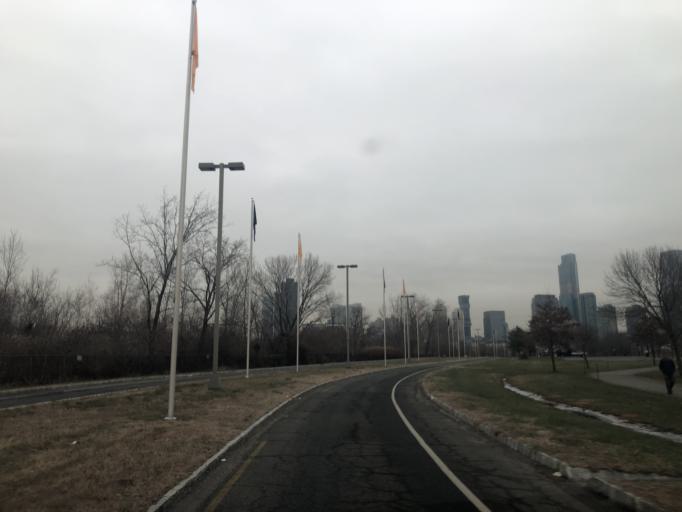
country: US
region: New Jersey
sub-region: Hudson County
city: Jersey City
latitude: 40.7040
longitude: -74.0475
